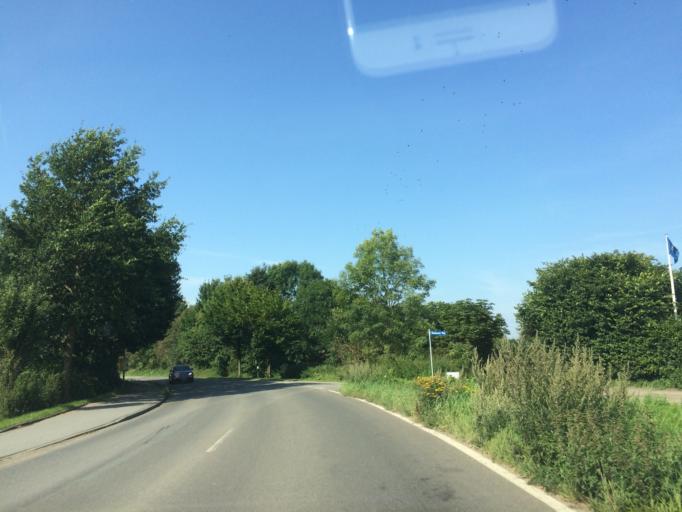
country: DE
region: Schleswig-Holstein
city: Honigsee
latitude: 54.2294
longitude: 10.1920
